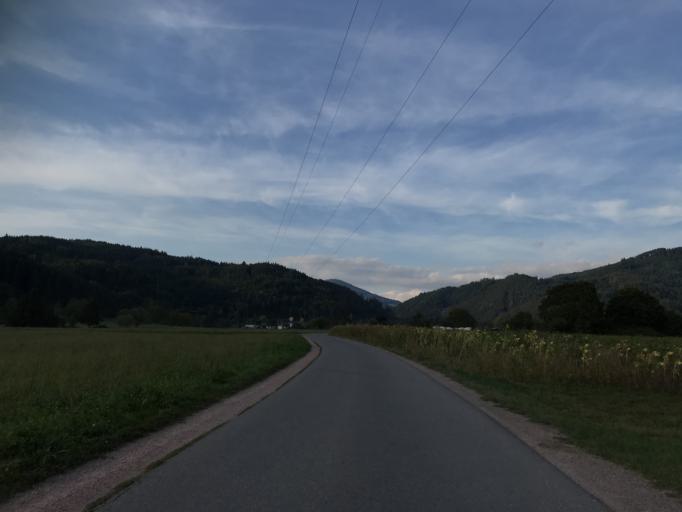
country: DE
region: Baden-Wuerttemberg
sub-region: Freiburg Region
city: Hausen
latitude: 47.6708
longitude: 7.8337
